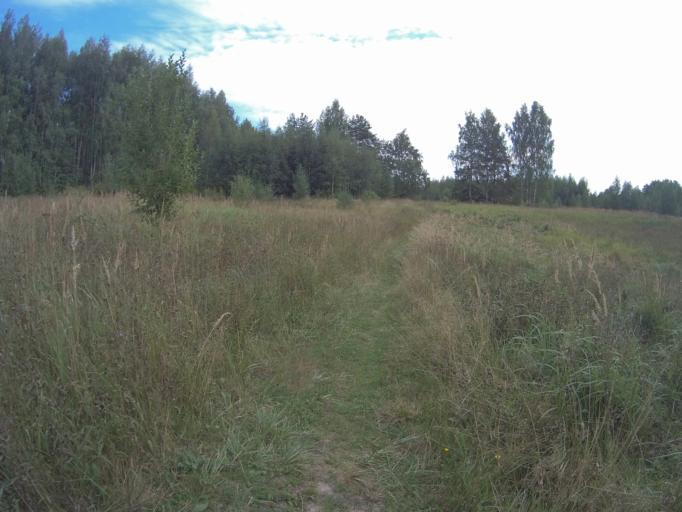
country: RU
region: Vladimir
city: Raduzhnyy
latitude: 56.0071
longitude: 40.3212
